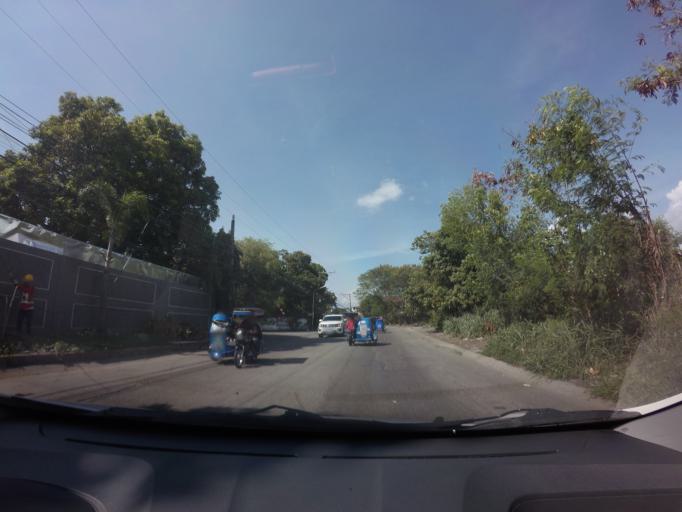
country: PH
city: Sambayanihan People's Village
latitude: 14.4460
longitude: 121.0080
